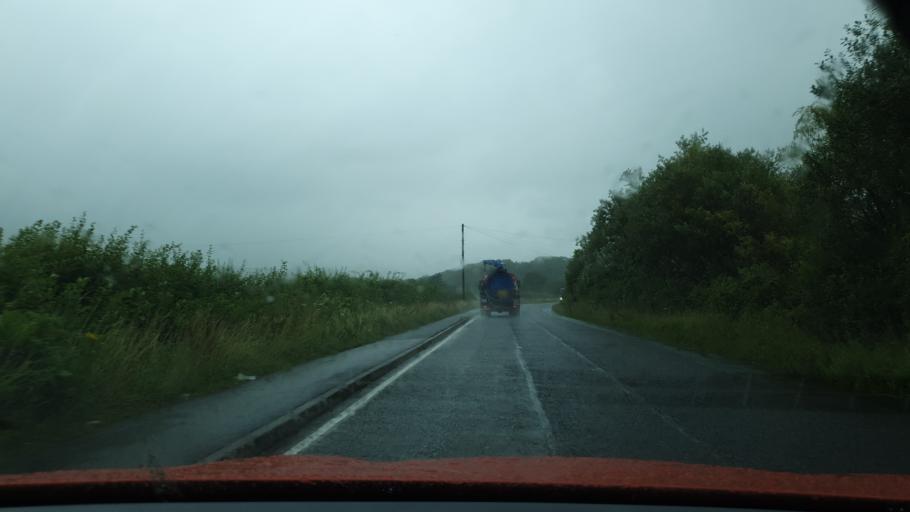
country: GB
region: England
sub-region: Cumbria
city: Millom
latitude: 54.2625
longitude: -3.2165
